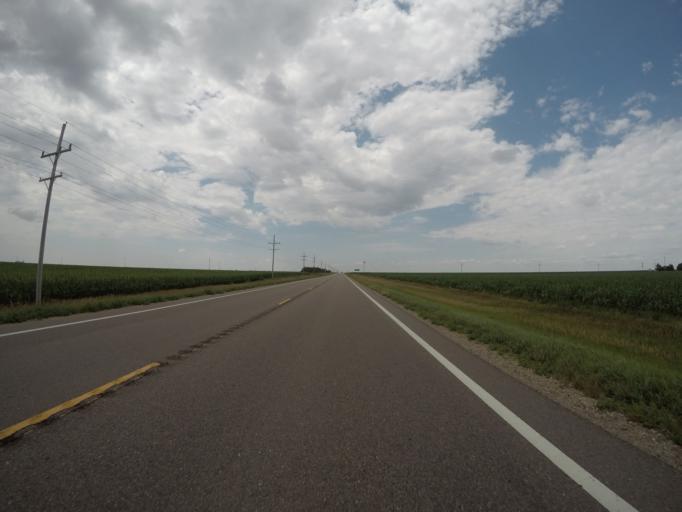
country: US
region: Kansas
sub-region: Thomas County
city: Colby
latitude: 39.3944
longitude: -100.9775
